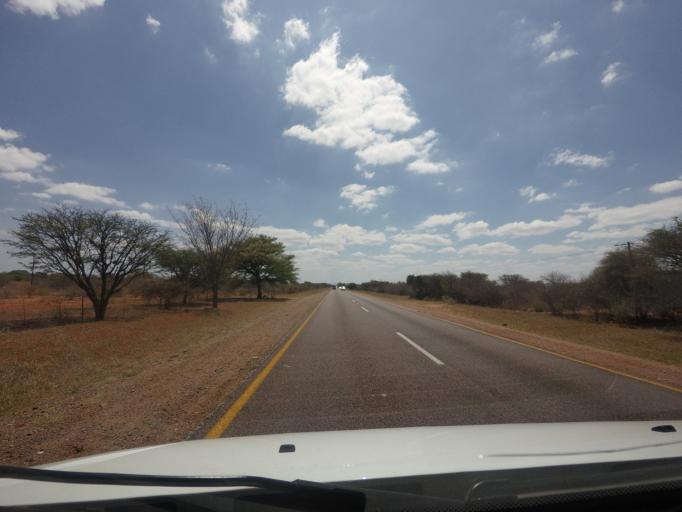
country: ZA
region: Limpopo
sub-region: Capricorn District Municipality
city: Dendron
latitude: -23.5474
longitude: 28.7278
